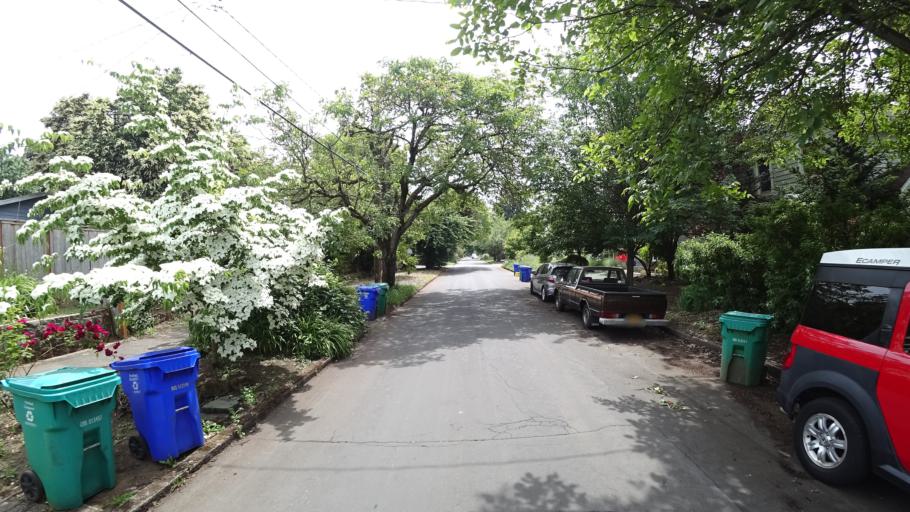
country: US
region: Oregon
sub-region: Washington County
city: West Haven
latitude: 45.5921
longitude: -122.7605
